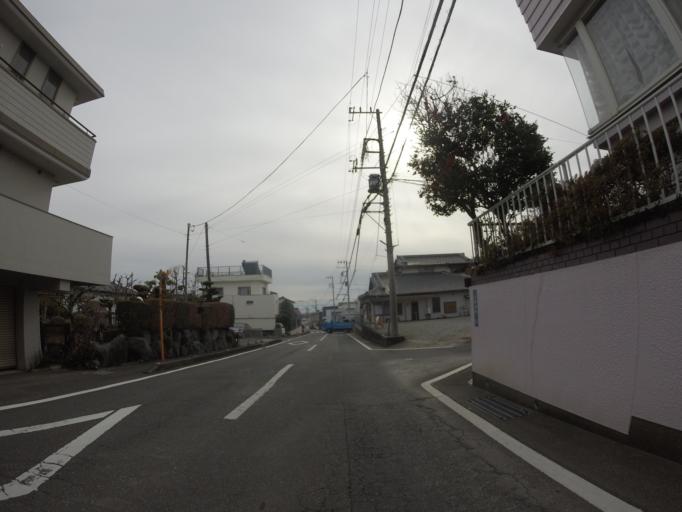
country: JP
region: Shizuoka
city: Fuji
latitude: 35.1855
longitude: 138.6887
